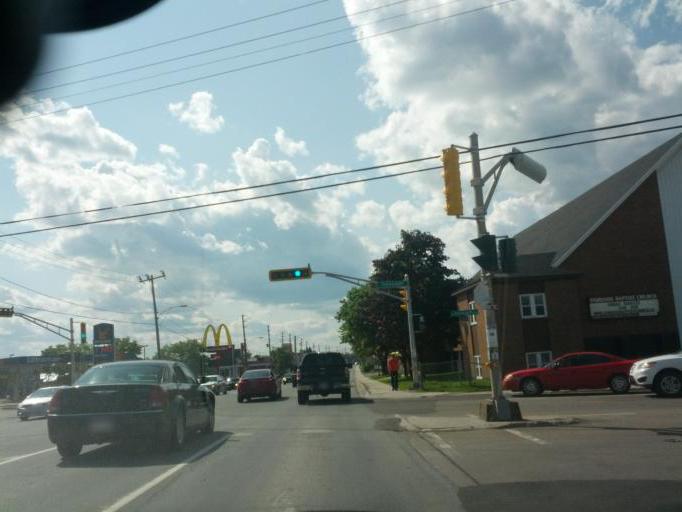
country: CA
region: New Brunswick
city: Moncton
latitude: 46.1007
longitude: -64.8104
